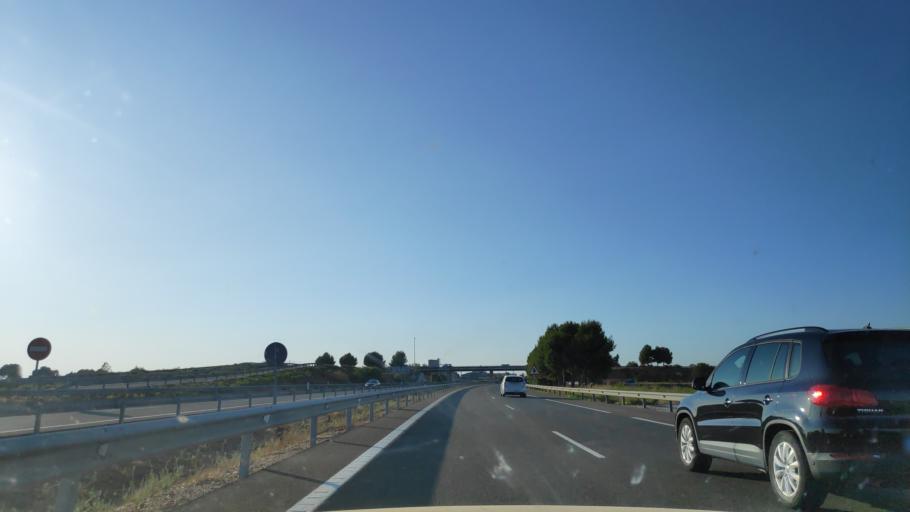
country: ES
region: Castille-La Mancha
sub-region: Provincia de Cuenca
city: Tarancon
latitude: 40.0028
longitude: -3.0255
